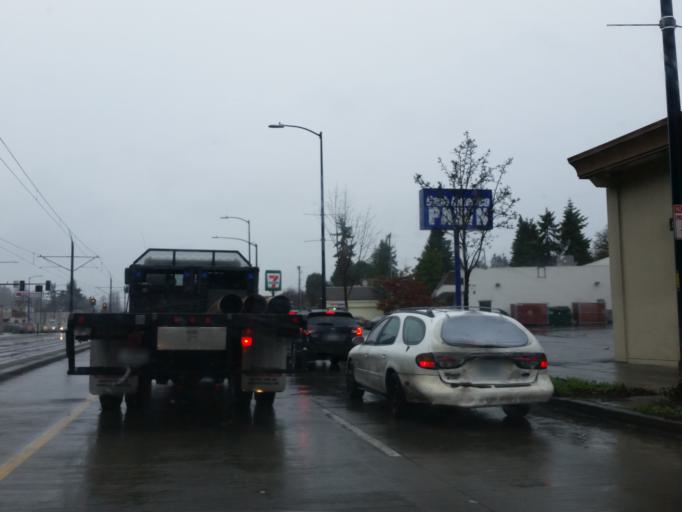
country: US
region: Washington
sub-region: King County
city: Riverton
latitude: 47.5504
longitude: -122.2876
